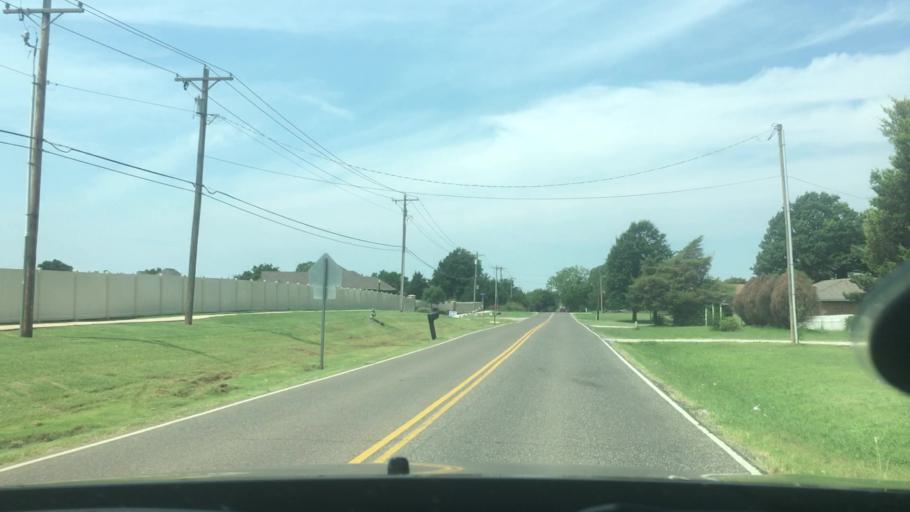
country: US
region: Oklahoma
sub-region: Pottawatomie County
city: Shawnee
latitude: 35.3617
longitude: -96.8964
